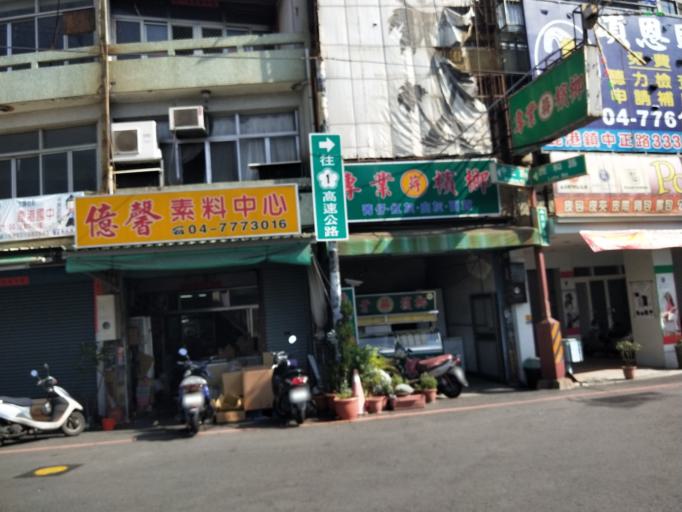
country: TW
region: Taiwan
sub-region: Changhua
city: Chang-hua
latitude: 24.0591
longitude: 120.4393
